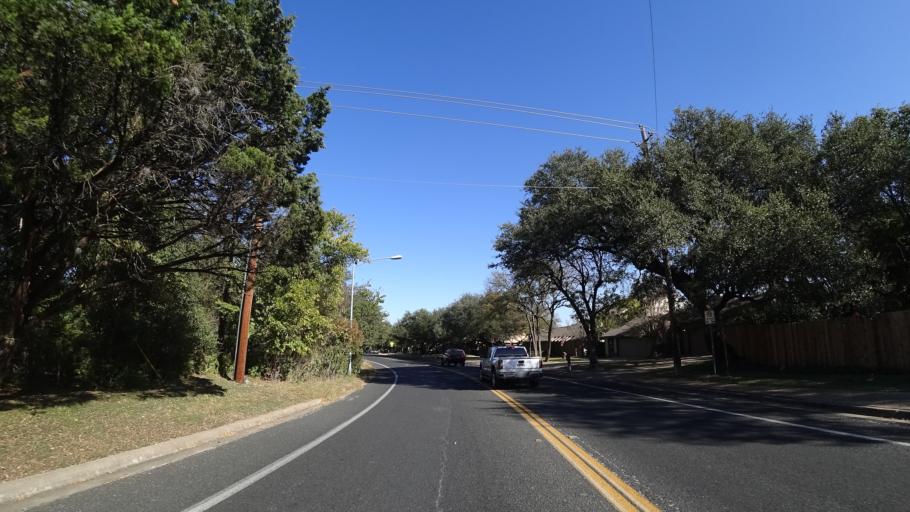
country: US
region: Texas
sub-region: Williamson County
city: Jollyville
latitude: 30.3726
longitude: -97.7514
